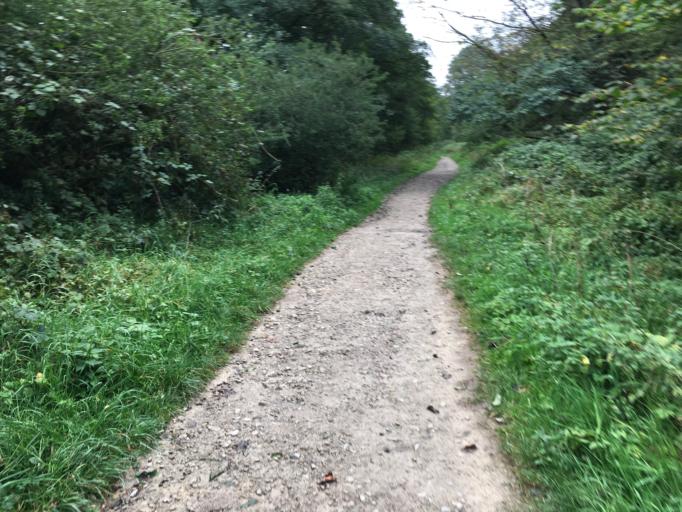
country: GB
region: England
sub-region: North Yorkshire
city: Sleights
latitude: 54.4069
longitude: -0.7341
